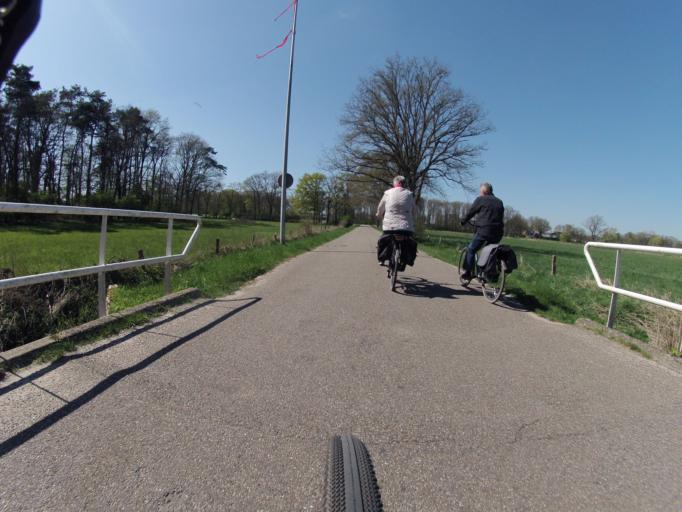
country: NL
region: Overijssel
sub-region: Gemeente Losser
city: Losser
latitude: 52.2693
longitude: 7.0275
